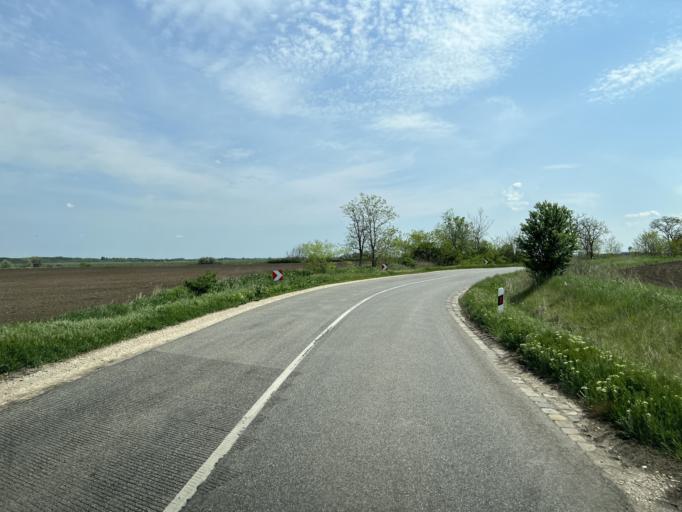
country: HU
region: Pest
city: Tapioszentmarton
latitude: 47.3147
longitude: 19.7576
